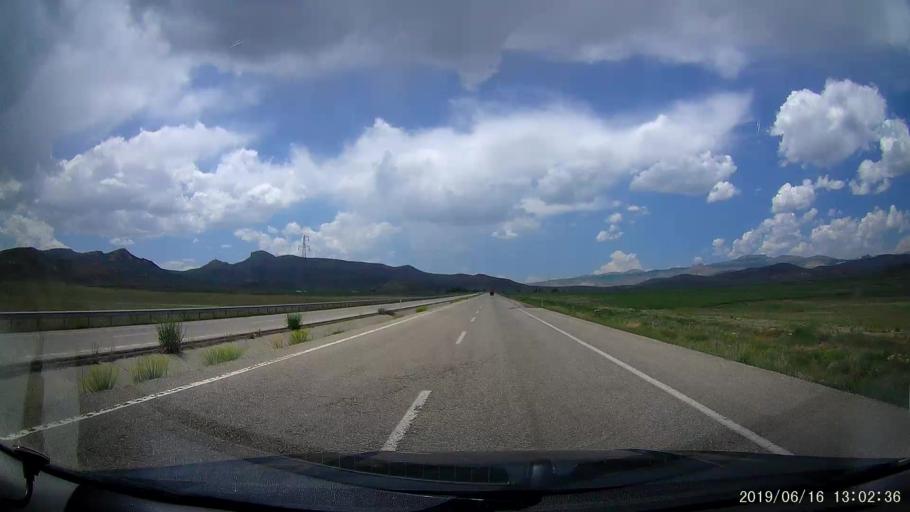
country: TR
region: Agri
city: Sulucem
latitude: 39.5756
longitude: 43.8116
